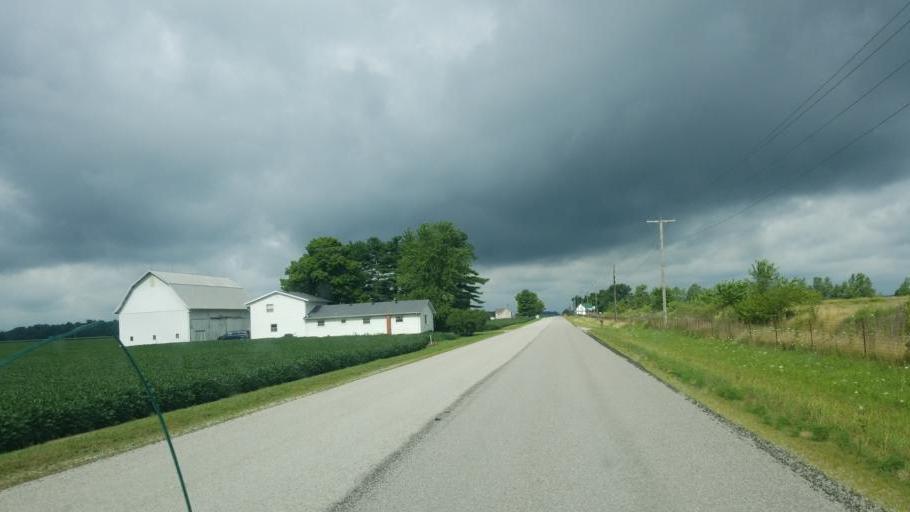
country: US
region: Indiana
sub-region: Adams County
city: Berne
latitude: 40.6557
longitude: -85.0566
